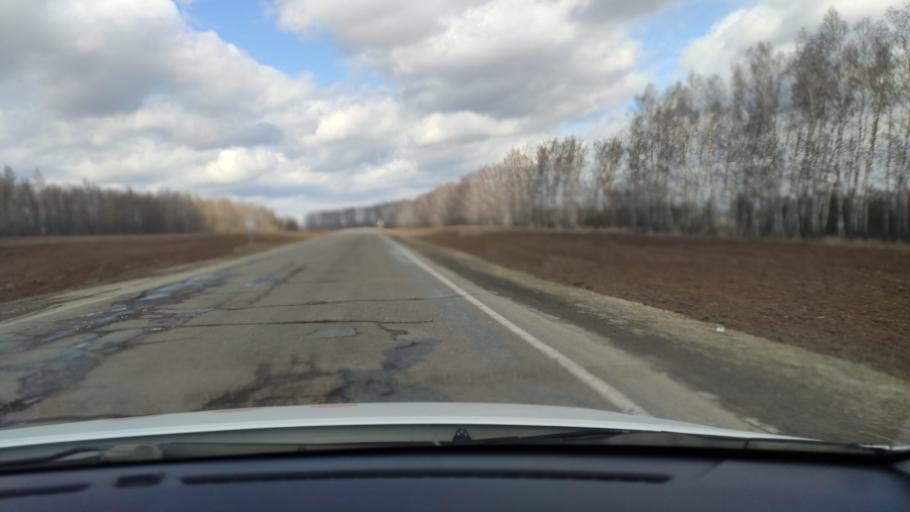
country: RU
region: Tatarstan
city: Vysokaya Gora
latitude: 56.0972
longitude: 49.1835
